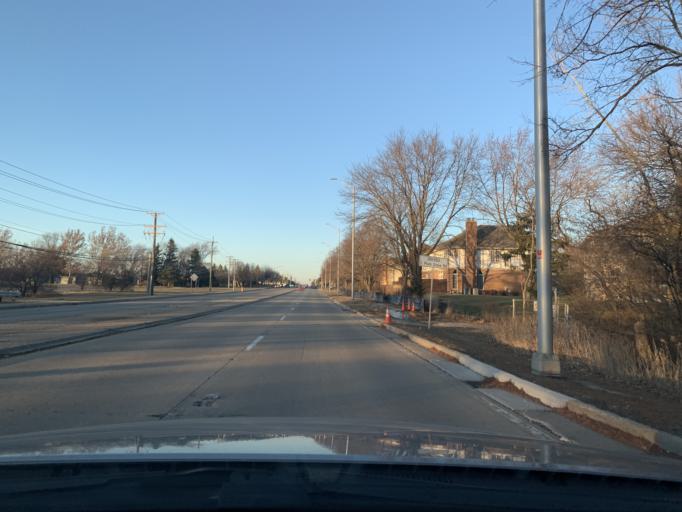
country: US
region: Illinois
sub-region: Cook County
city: Schaumburg
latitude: 42.0247
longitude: -88.0603
